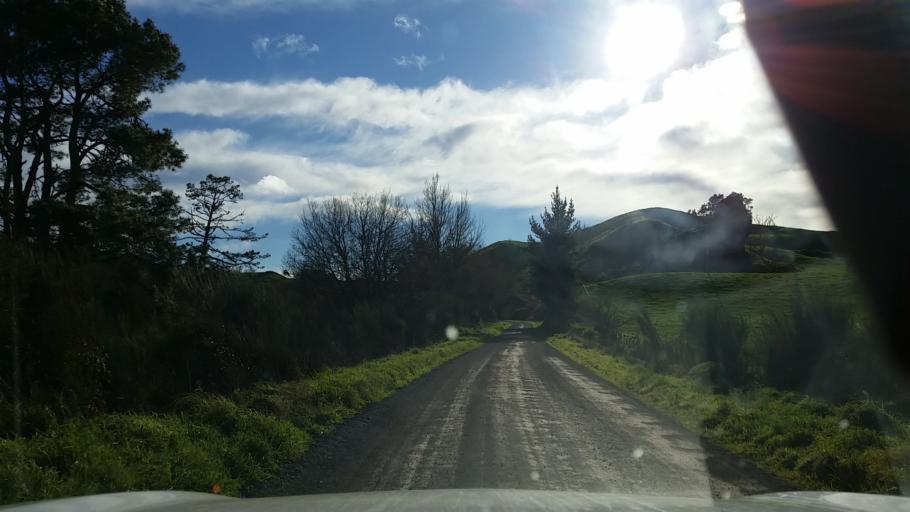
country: NZ
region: Waikato
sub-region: South Waikato District
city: Tokoroa
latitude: -38.3752
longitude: 176.0859
